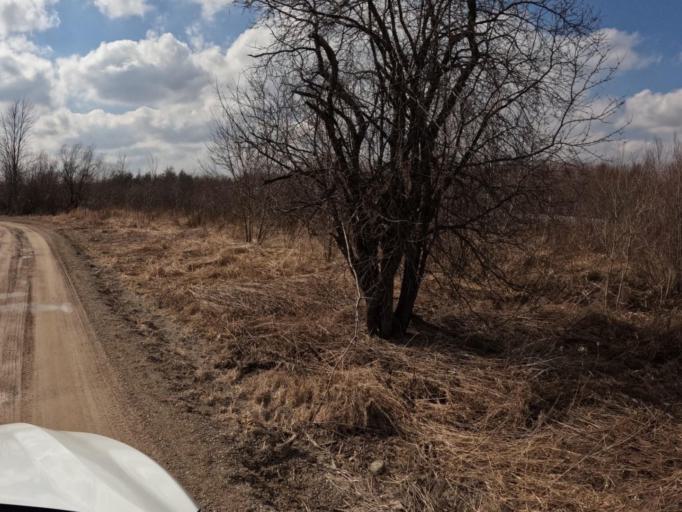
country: CA
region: Ontario
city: Shelburne
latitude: 43.9686
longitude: -80.2743
